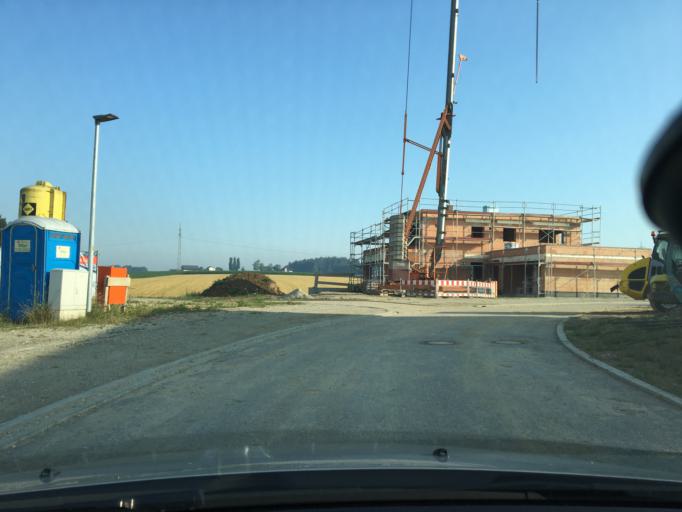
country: DE
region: Bavaria
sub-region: Lower Bavaria
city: Vilsbiburg
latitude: 48.4579
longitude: 12.3464
